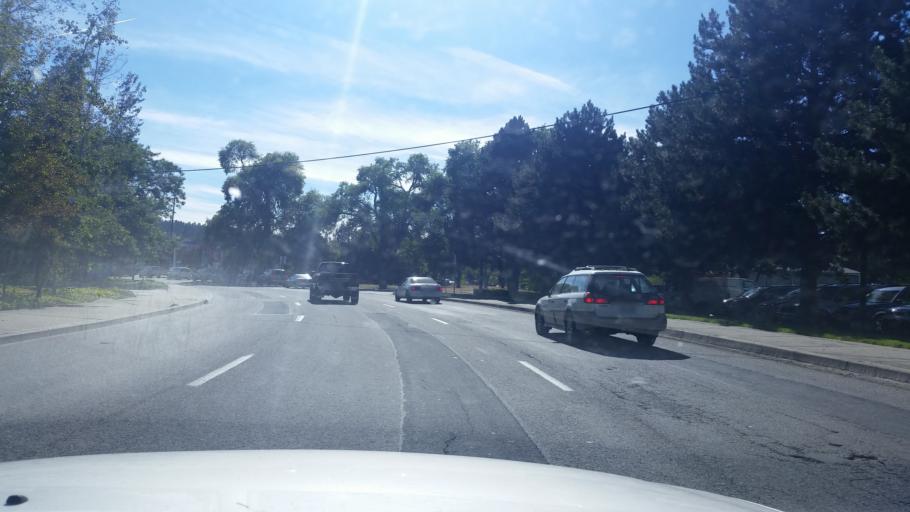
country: US
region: Washington
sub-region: Spokane County
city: Spokane
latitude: 47.6557
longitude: -117.3594
